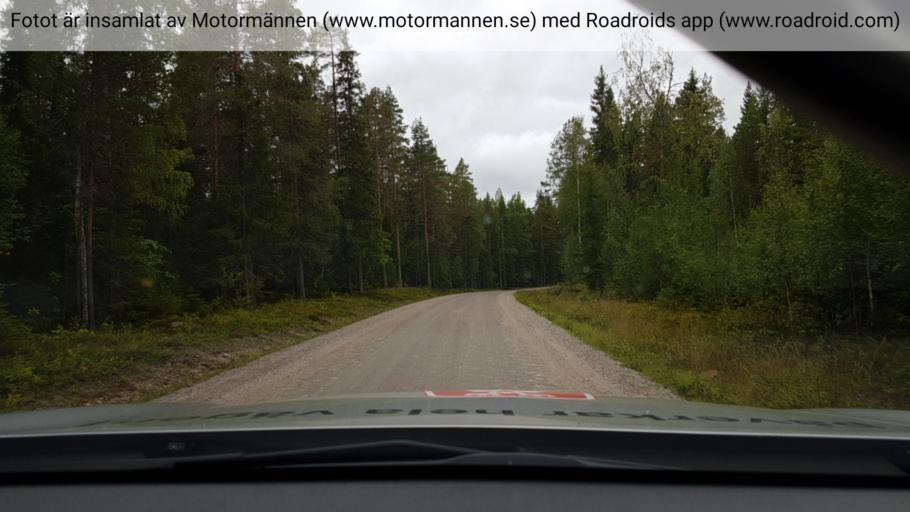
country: SE
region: Vaesterbotten
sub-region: Skelleftea Kommun
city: Forsbacka
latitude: 64.7506
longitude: 20.4402
